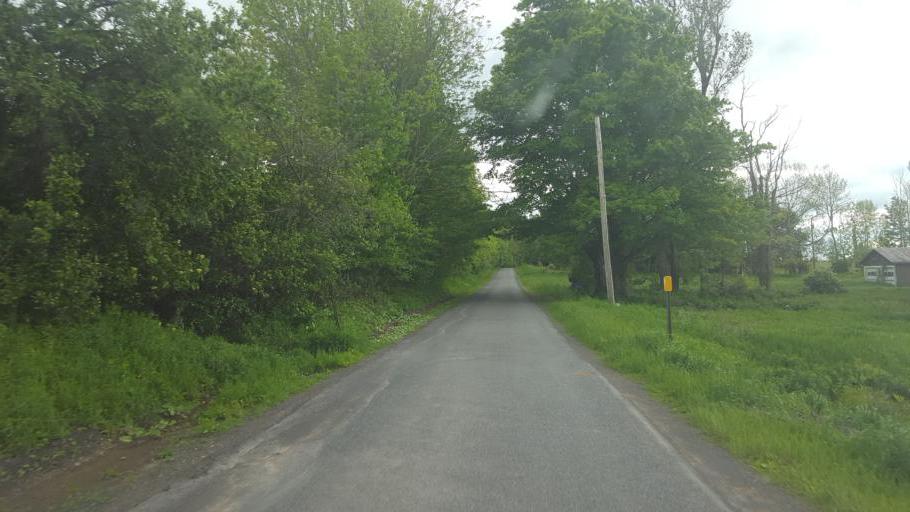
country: US
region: New York
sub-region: Otsego County
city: Richfield Springs
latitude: 42.8616
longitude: -74.9567
